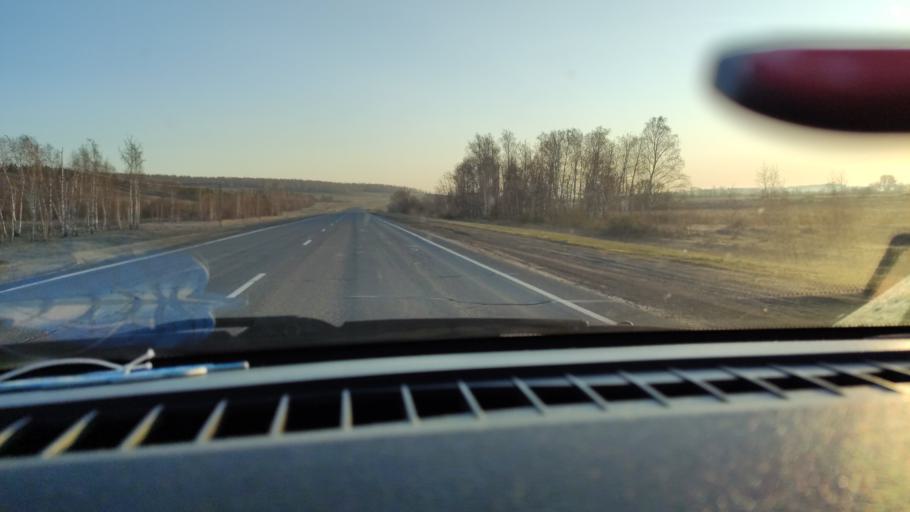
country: RU
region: Saratov
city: Sinodskoye
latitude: 52.0616
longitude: 46.7642
